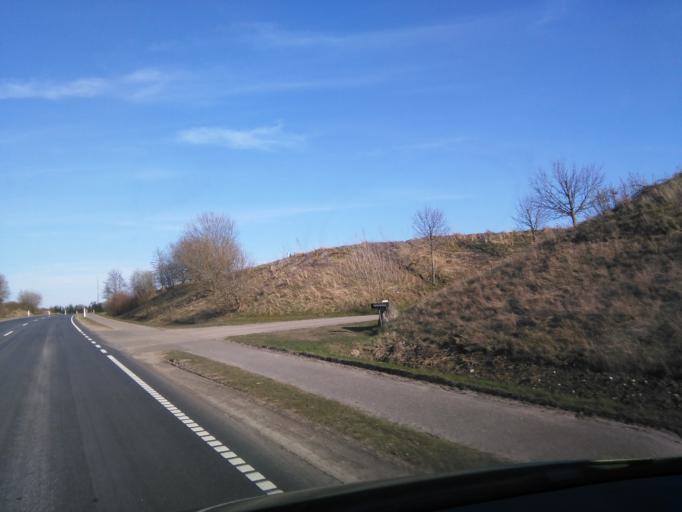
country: DK
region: Central Jutland
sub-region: Horsens Kommune
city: Braedstrup
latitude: 55.9652
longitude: 9.7281
